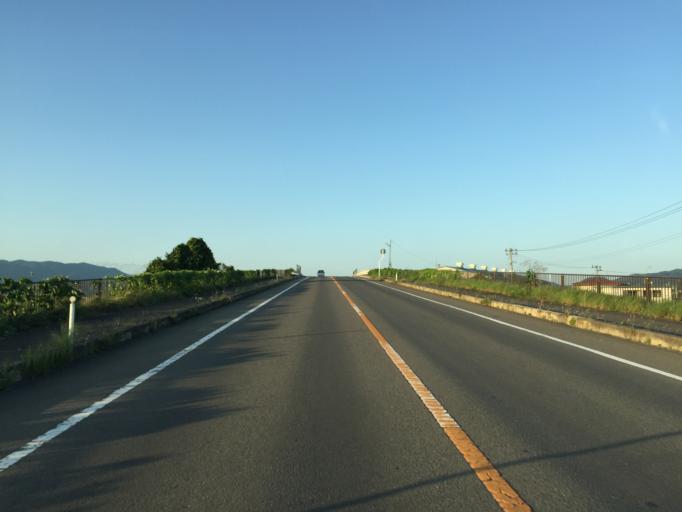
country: JP
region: Fukushima
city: Yanagawamachi-saiwaicho
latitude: 37.8414
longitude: 140.5988
